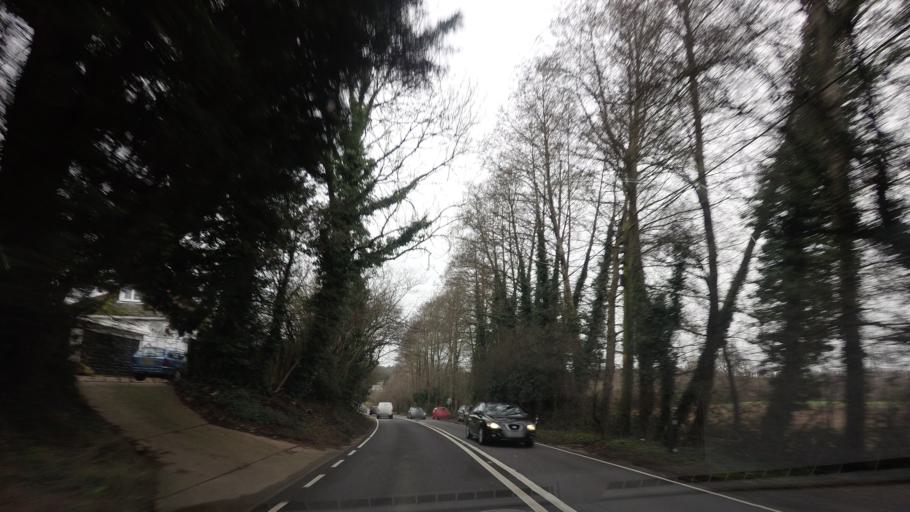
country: GB
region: England
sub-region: East Sussex
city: Saint Leonards-on-Sea
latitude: 50.9122
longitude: 0.5437
